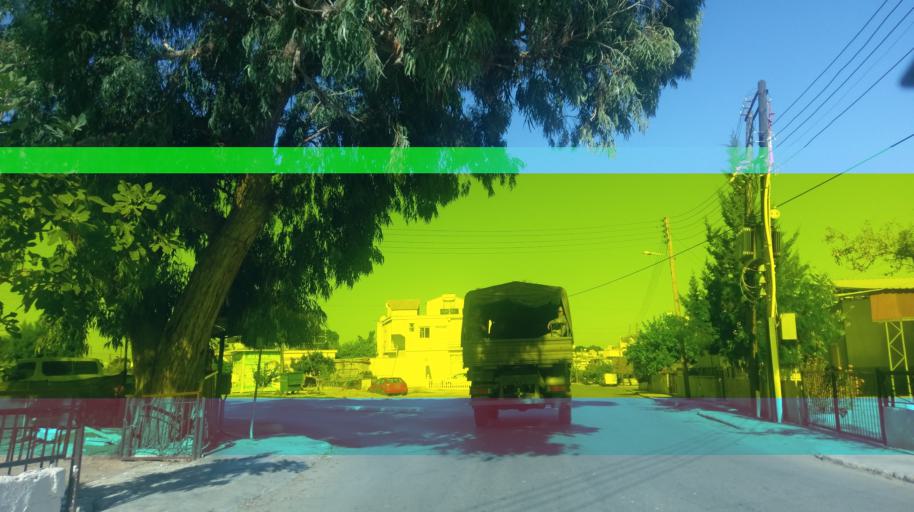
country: CY
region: Ammochostos
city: Famagusta
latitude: 35.1035
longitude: 33.9468
